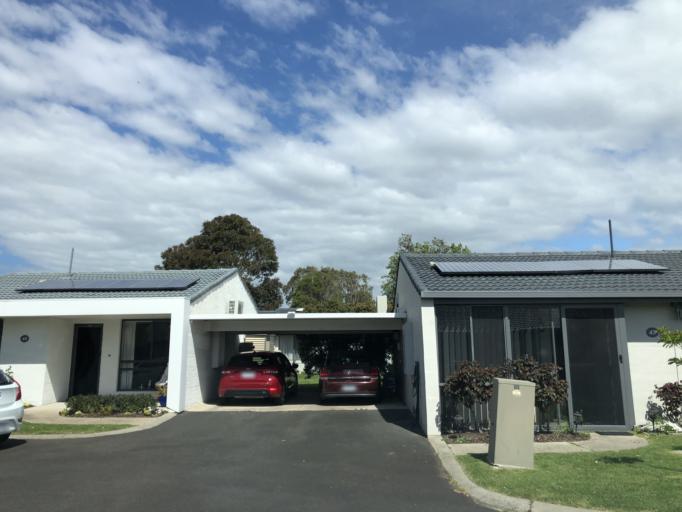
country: AU
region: Victoria
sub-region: Kingston
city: Patterson Lakes
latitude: -38.0714
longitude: 145.1394
